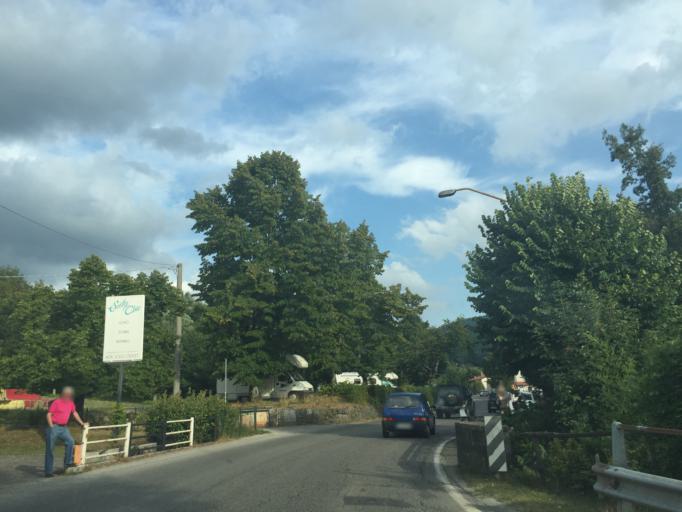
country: IT
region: Tuscany
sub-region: Provincia di Pistoia
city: San Marcello Pistoiese
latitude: 44.0537
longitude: 10.8013
